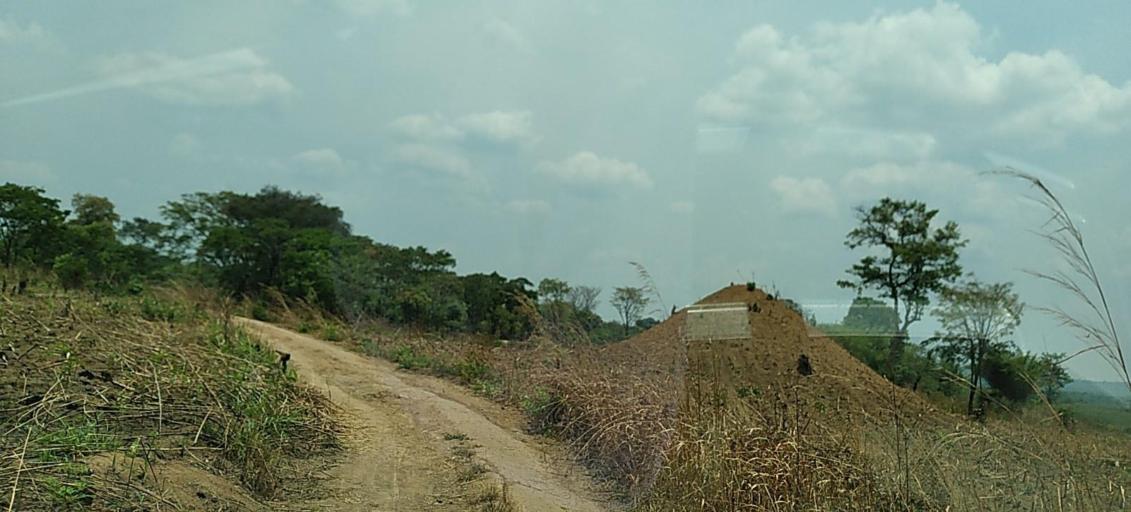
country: ZM
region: Copperbelt
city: Chililabombwe
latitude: -12.3769
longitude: 27.6432
